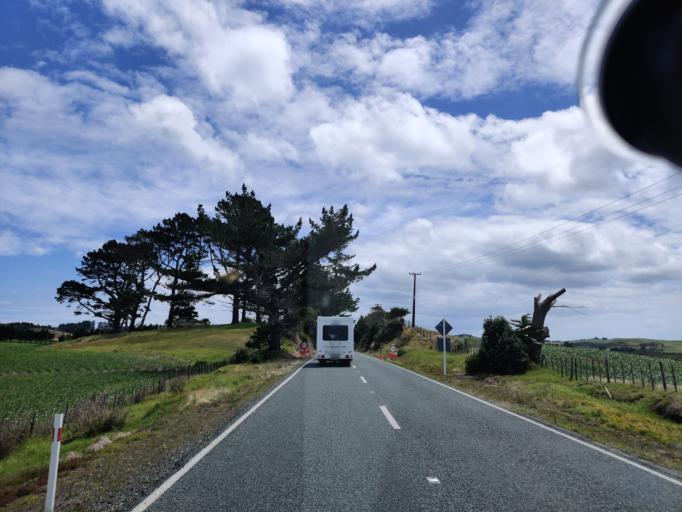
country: NZ
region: Northland
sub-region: Far North District
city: Kaitaia
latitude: -34.7788
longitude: 173.0941
